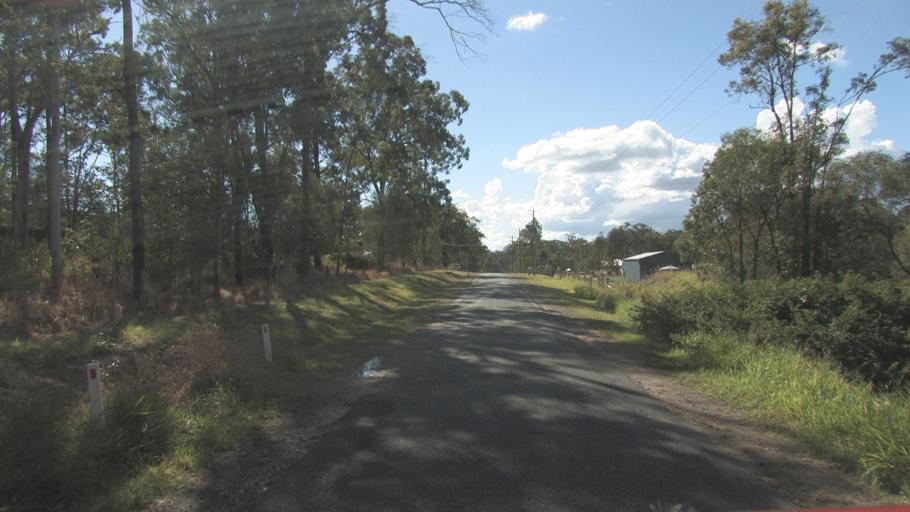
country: AU
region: Queensland
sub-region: Logan
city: Chambers Flat
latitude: -27.8072
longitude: 153.0824
